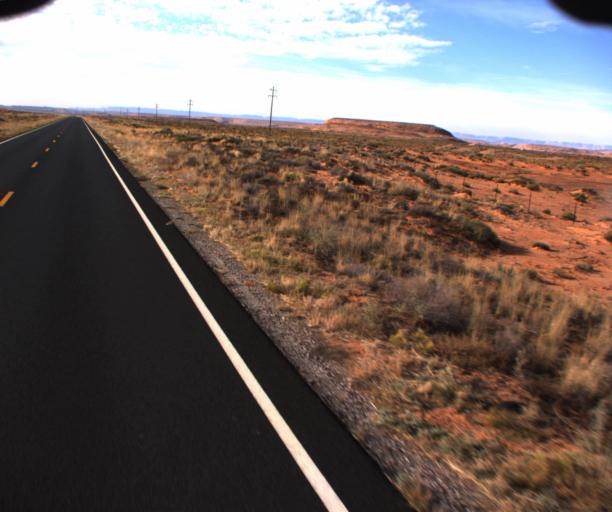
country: US
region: Arizona
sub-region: Apache County
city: Many Farms
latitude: 36.8460
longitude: -109.6399
